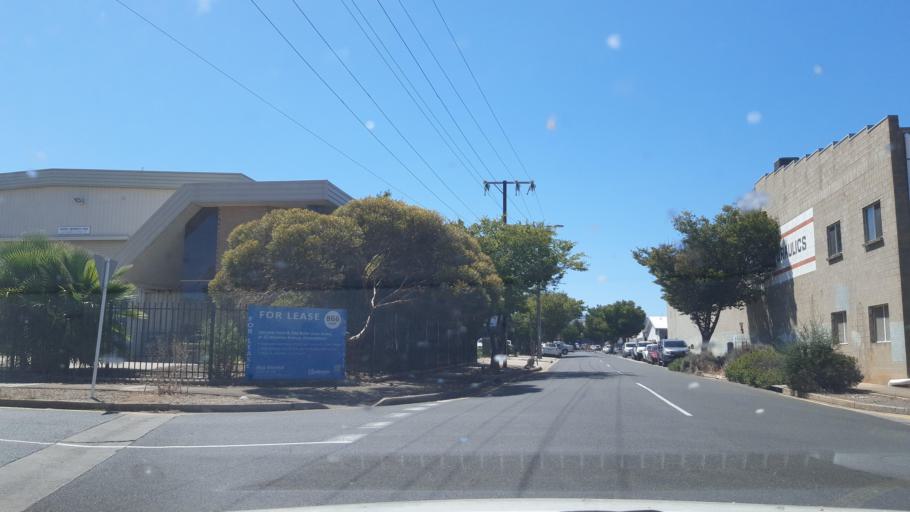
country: AU
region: South Australia
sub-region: Marion
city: Clovelly Park
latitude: -34.9878
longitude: 138.5706
